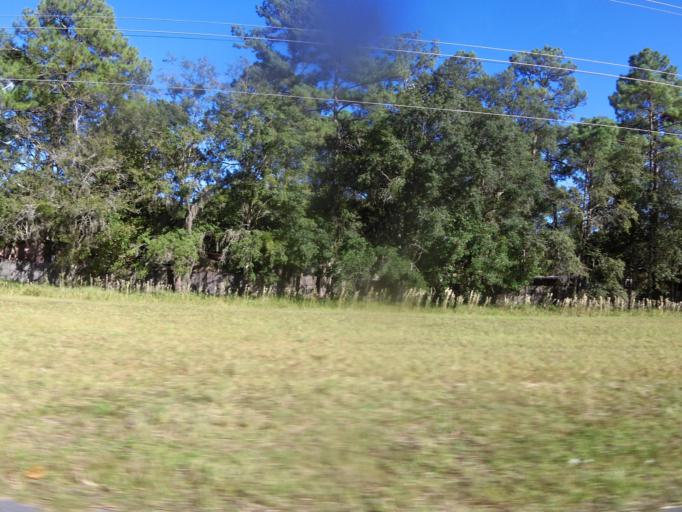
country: US
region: Florida
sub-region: Alachua County
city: Alachua
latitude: 29.7339
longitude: -82.3888
